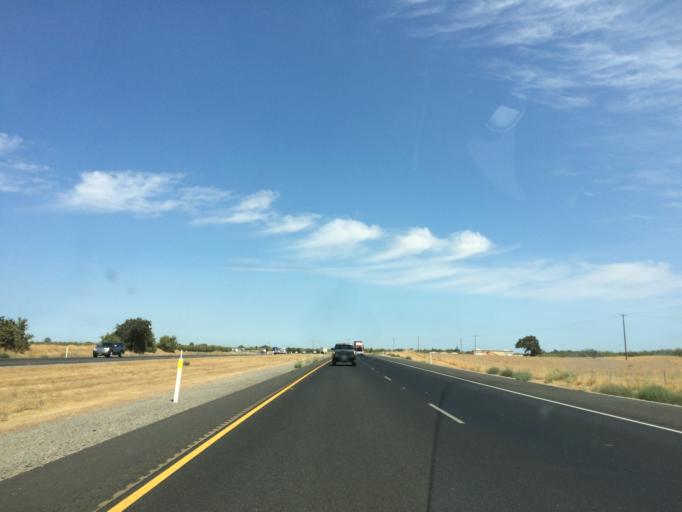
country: US
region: California
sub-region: Colusa County
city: Arbuckle
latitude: 38.9701
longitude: -122.0277
